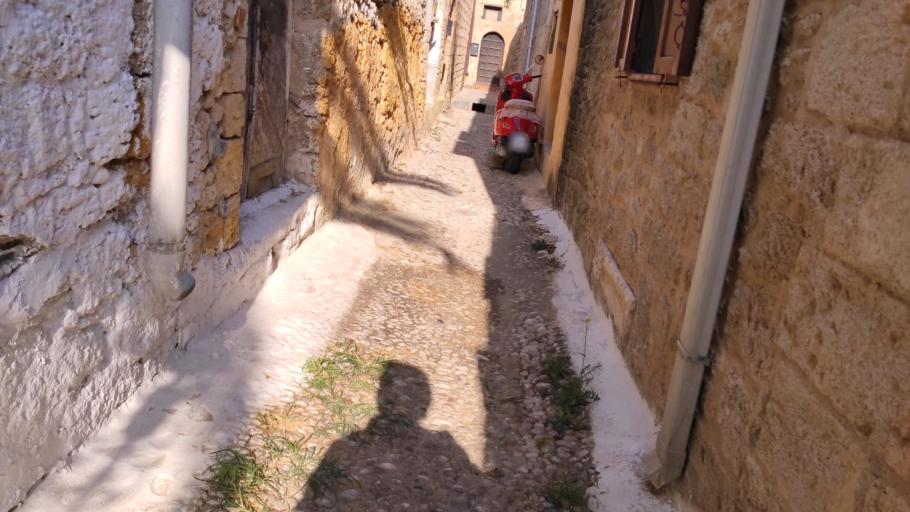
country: GR
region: South Aegean
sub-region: Nomos Dodekanisou
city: Rodos
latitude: 36.4435
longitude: 28.2229
